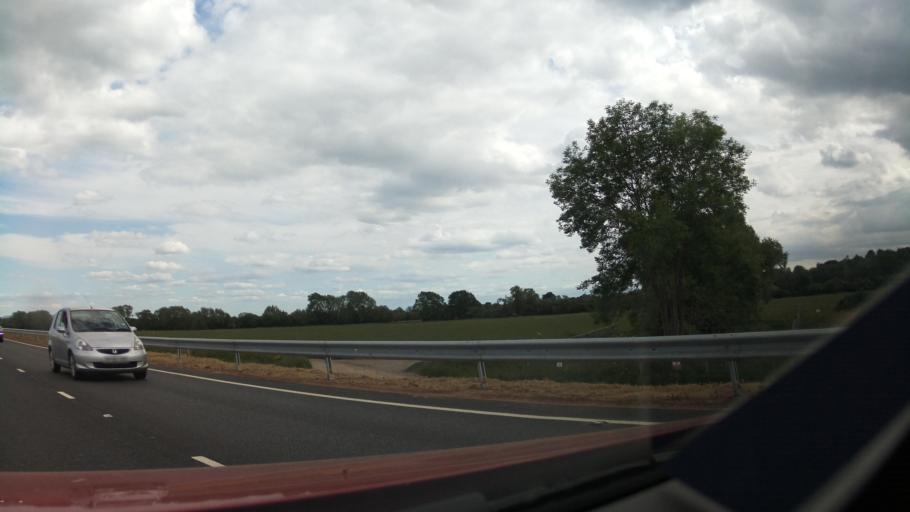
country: GB
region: England
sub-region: Worcestershire
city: Worcester
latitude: 52.1670
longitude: -2.2391
